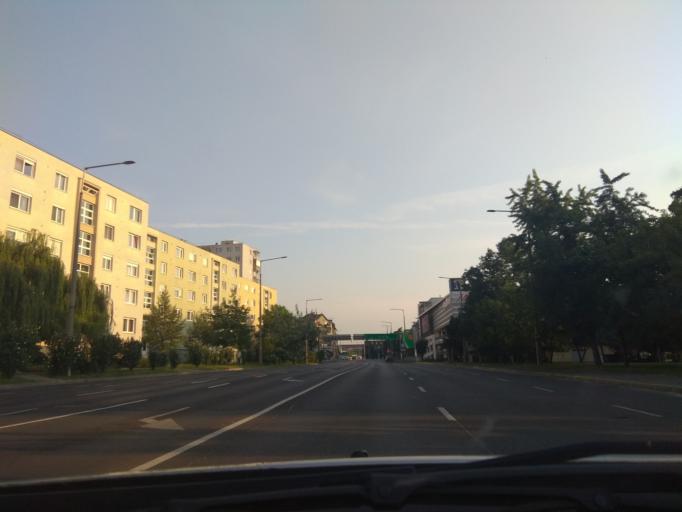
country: HU
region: Borsod-Abauj-Zemplen
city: Miskolc
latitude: 48.1002
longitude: 20.7923
